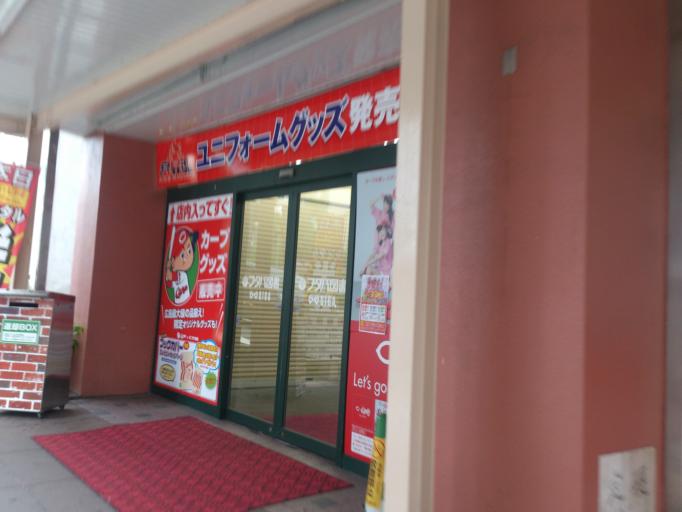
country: JP
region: Hiroshima
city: Hiroshima-shi
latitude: 34.3963
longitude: 132.4764
